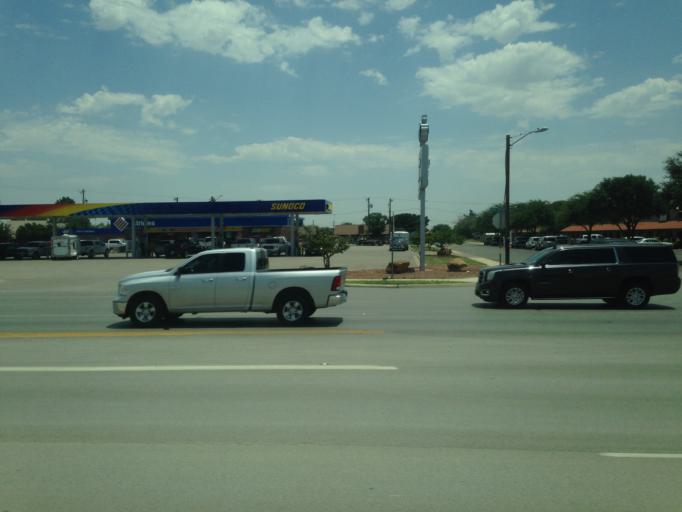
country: US
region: Texas
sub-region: Midland County
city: Midland
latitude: 32.0429
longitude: -102.0857
